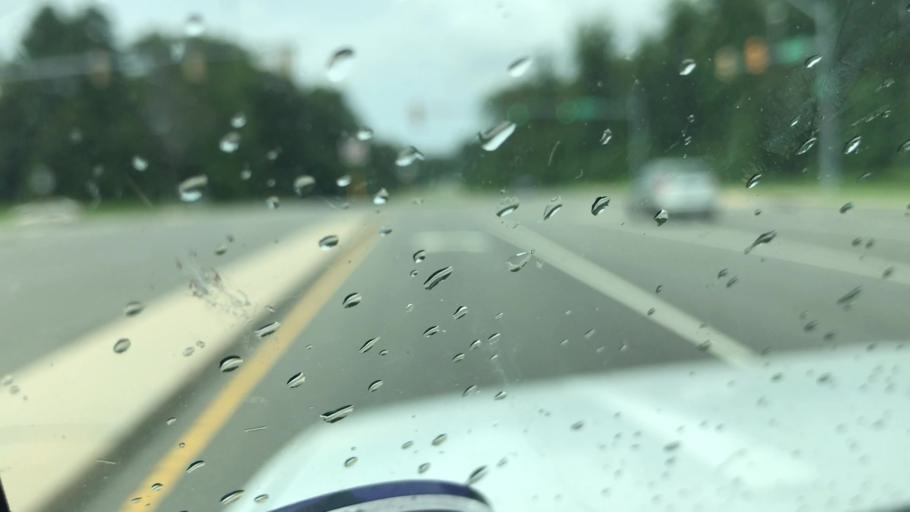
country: US
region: Virginia
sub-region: Henrico County
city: Short Pump
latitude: 37.6352
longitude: -77.6132
